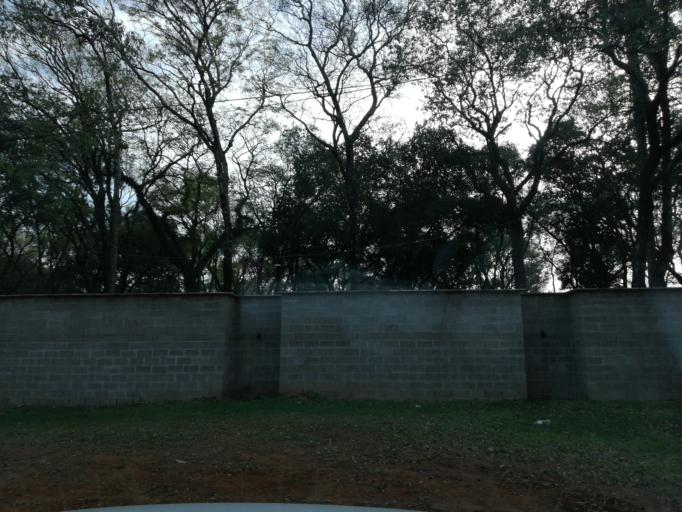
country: AR
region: Misiones
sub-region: Departamento de Capital
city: Posadas
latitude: -27.3544
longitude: -55.9261
